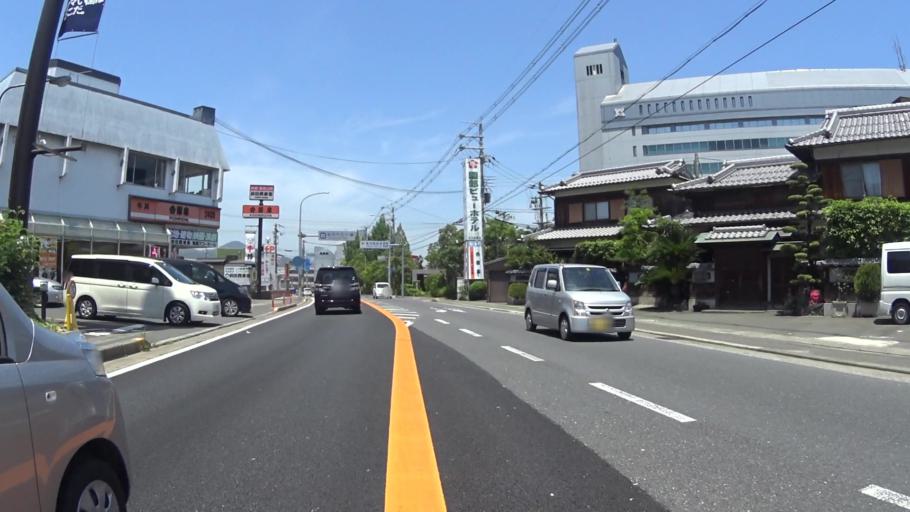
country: JP
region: Kyoto
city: Kameoka
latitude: 35.0124
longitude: 135.5735
